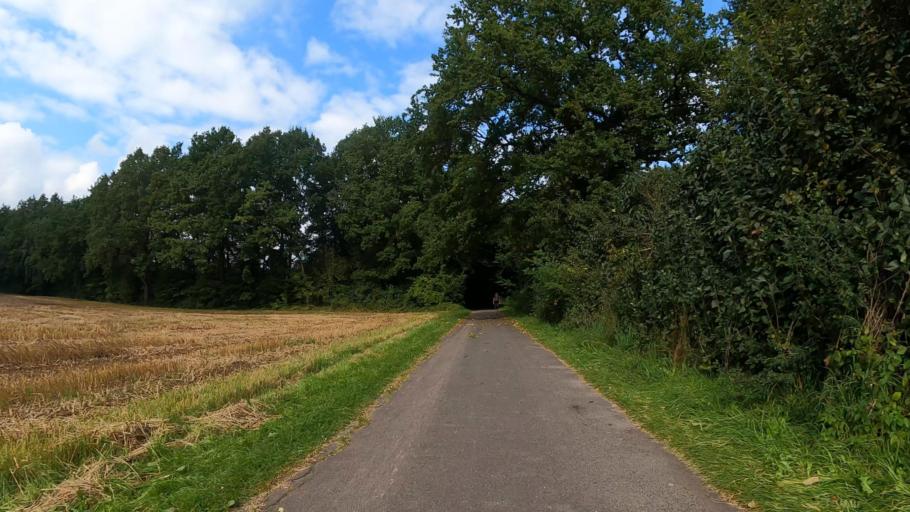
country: DE
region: Schleswig-Holstein
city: Kolln-Reisiek
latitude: 53.7266
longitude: 9.6842
